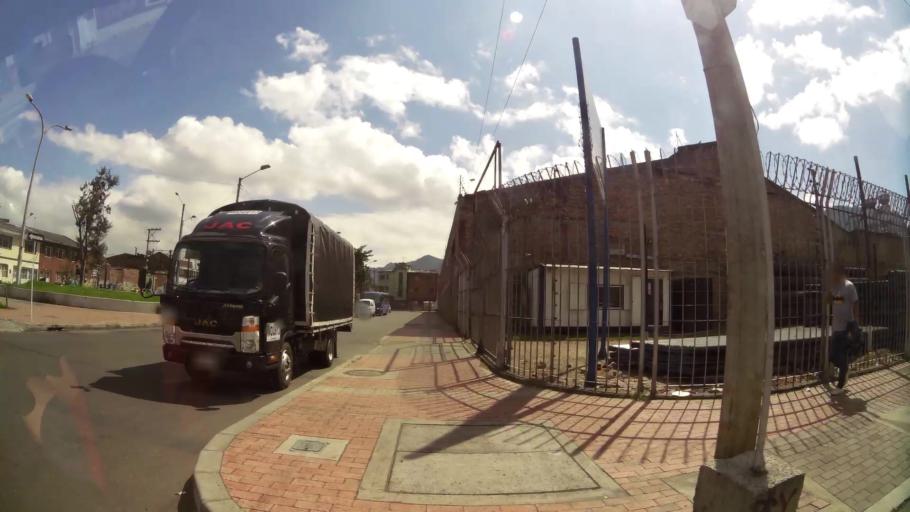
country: CO
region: Bogota D.C.
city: Bogota
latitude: 4.6171
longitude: -74.0800
